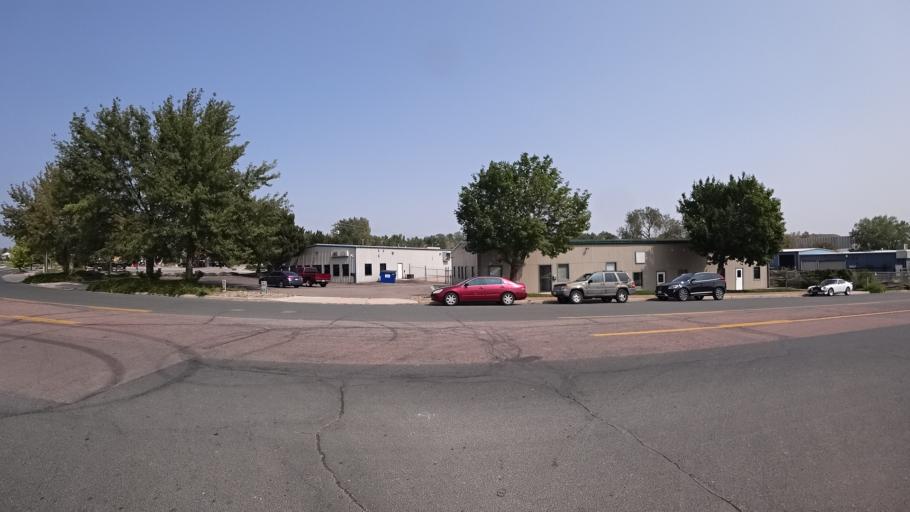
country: US
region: Colorado
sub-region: El Paso County
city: Stratmoor
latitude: 38.7957
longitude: -104.7774
